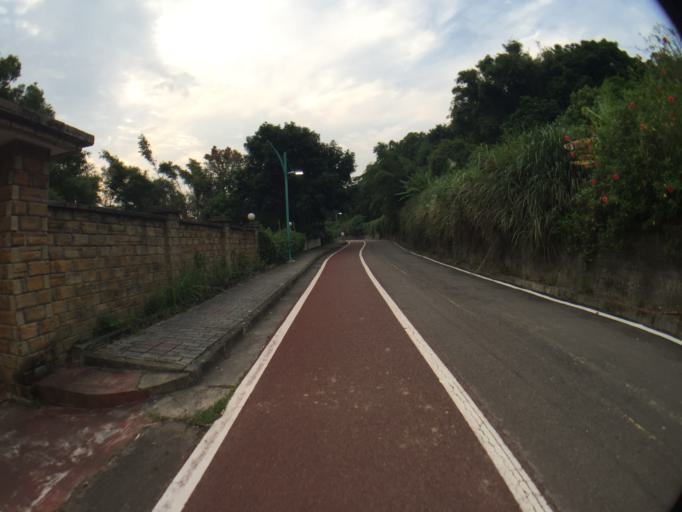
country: TW
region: Taiwan
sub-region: Hsinchu
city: Hsinchu
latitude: 24.7729
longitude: 120.9767
